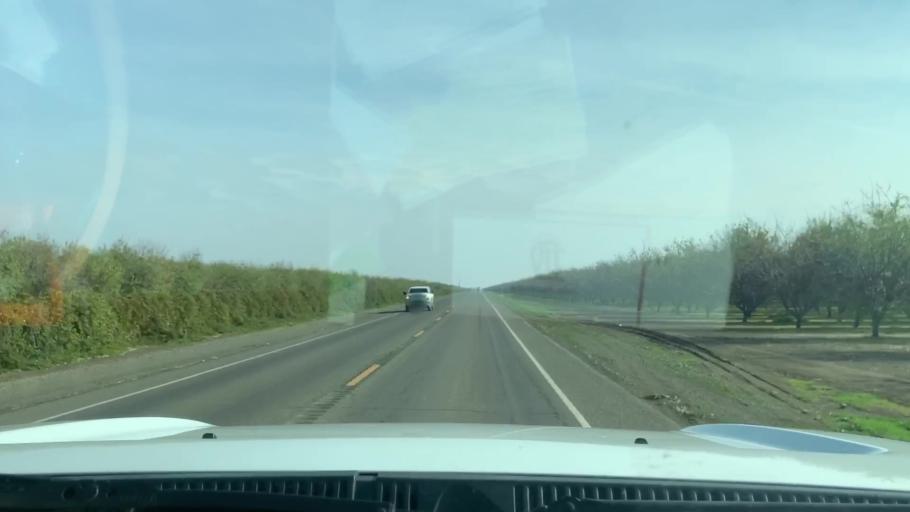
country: US
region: California
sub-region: Fresno County
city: Huron
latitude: 36.2552
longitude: -120.1340
